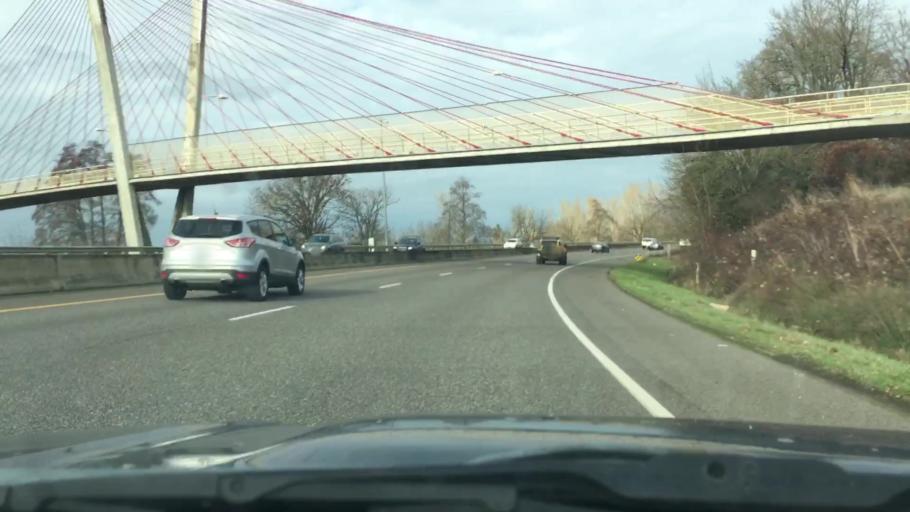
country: US
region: Oregon
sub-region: Lane County
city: Eugene
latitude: 44.0757
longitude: -123.1054
